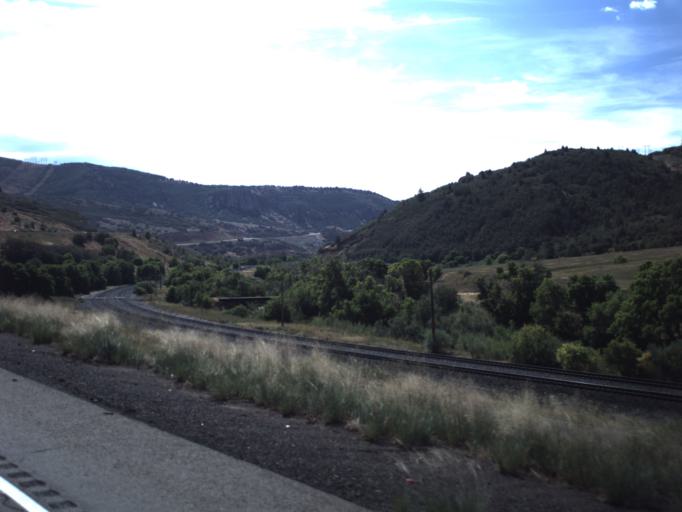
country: US
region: Utah
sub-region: Utah County
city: Mapleton
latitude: 40.0342
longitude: -111.5195
